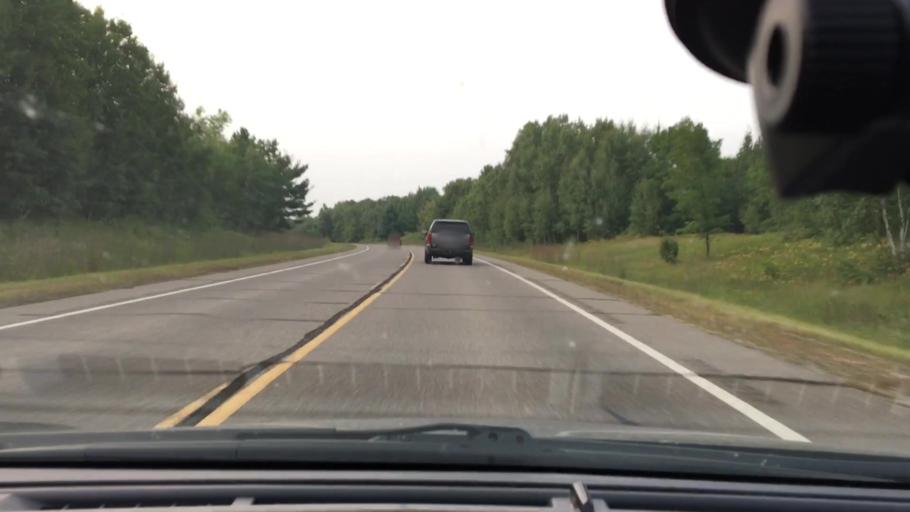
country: US
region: Minnesota
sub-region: Crow Wing County
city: Crosby
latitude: 46.4345
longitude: -93.8737
